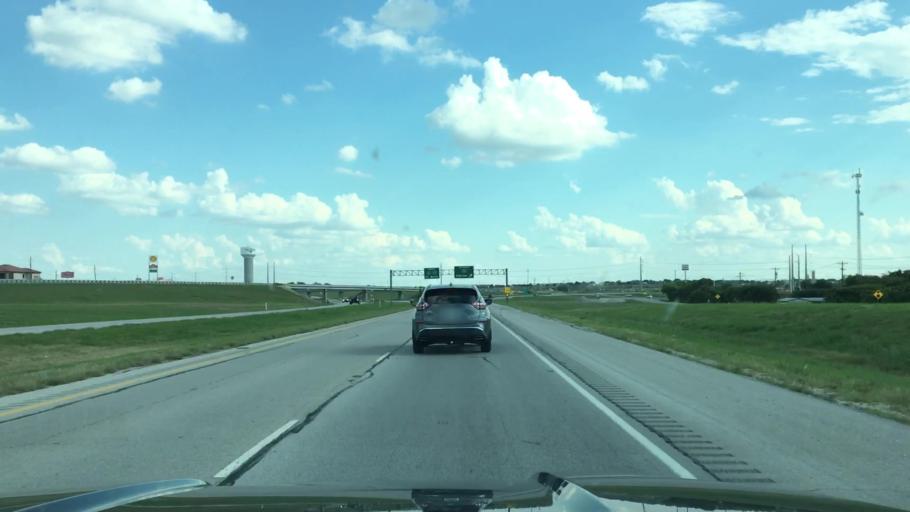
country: US
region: Texas
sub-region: Tarrant County
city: Pecan Acres
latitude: 32.9731
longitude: -97.4221
